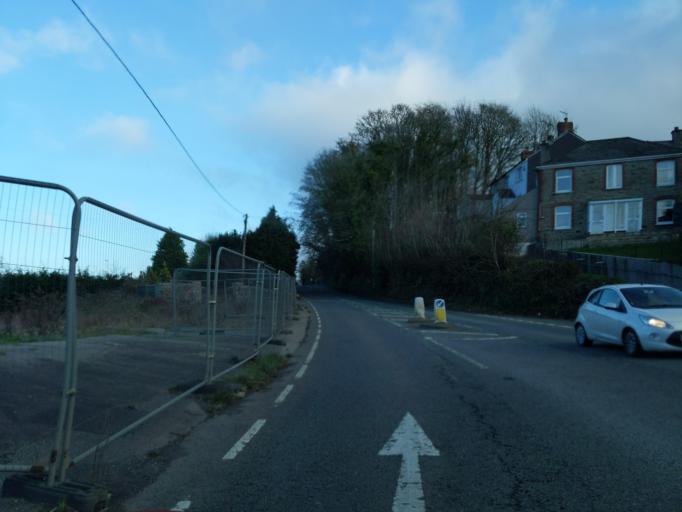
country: GB
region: England
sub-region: Cornwall
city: Pillaton
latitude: 50.3888
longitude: -4.3248
